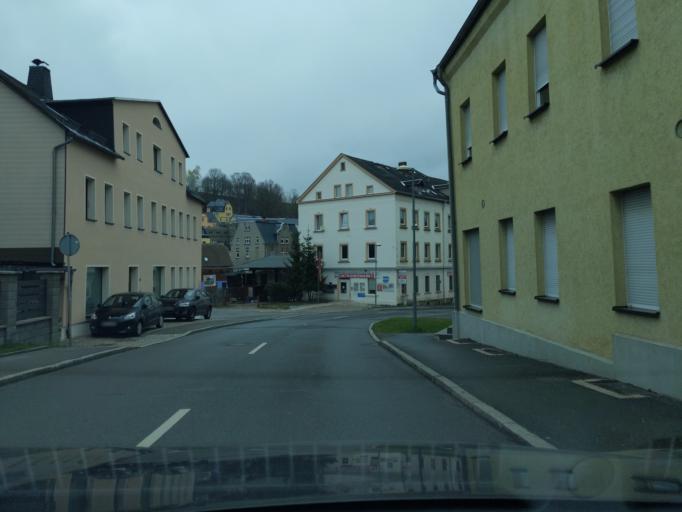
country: DE
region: Saxony
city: Schneeberg
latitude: 50.5871
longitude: 12.6354
